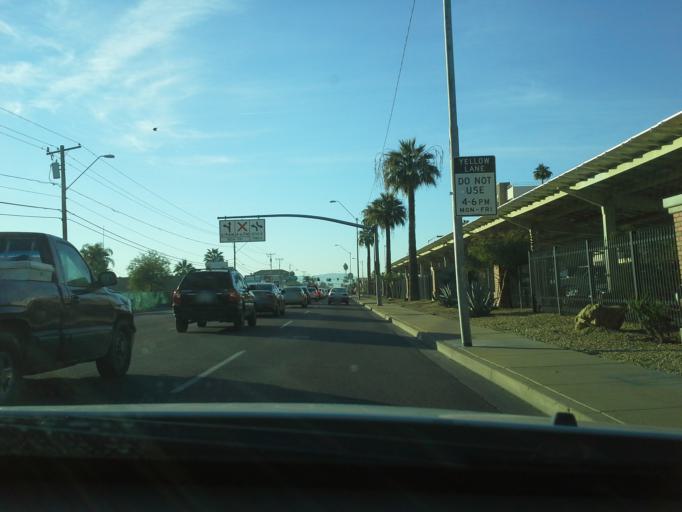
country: US
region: Arizona
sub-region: Maricopa County
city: Phoenix
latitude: 33.4972
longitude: -112.0651
